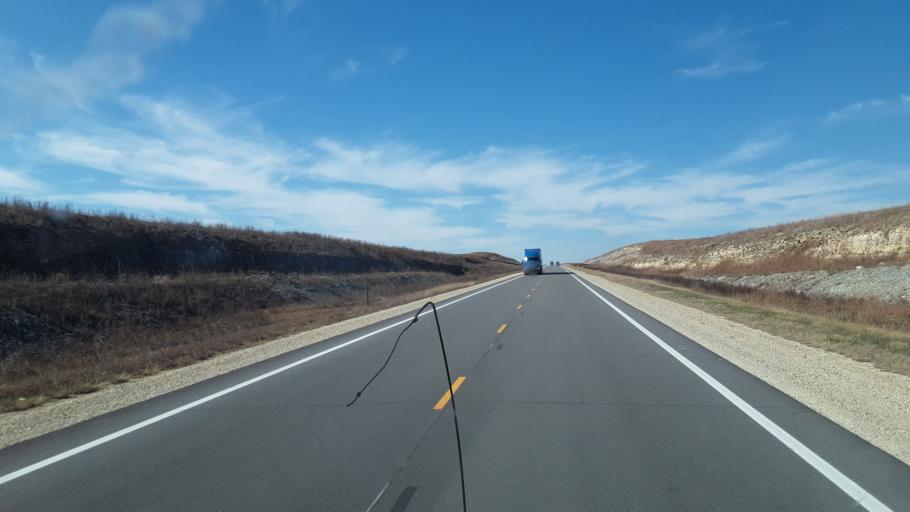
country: US
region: Kansas
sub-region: Chase County
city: Cottonwood Falls
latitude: 38.3627
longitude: -96.6871
